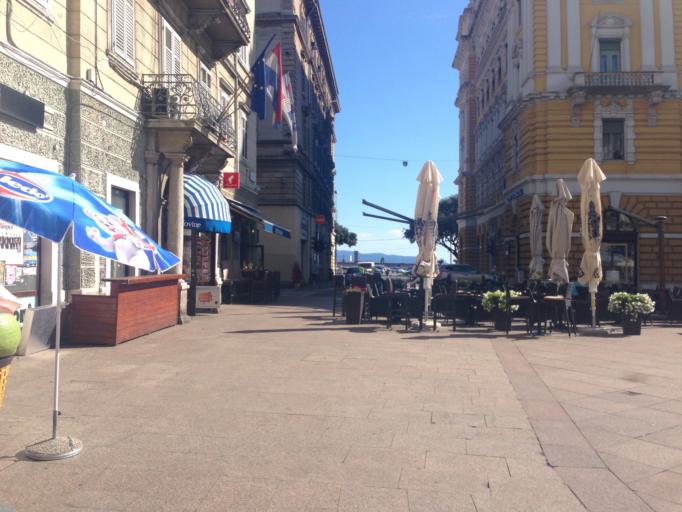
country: HR
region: Primorsko-Goranska
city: Drenova
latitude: 45.3277
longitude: 14.4394
